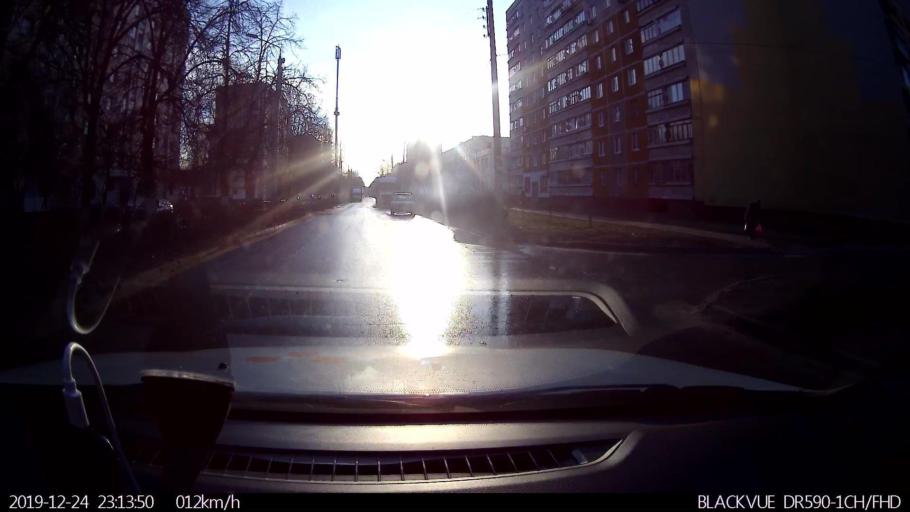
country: RU
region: Nizjnij Novgorod
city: Gorbatovka
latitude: 56.2524
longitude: 43.8590
